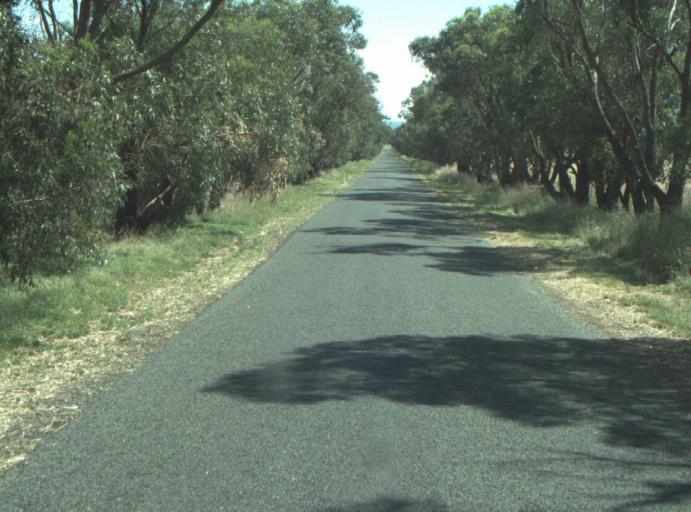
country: AU
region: Victoria
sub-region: Greater Geelong
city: Leopold
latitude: -38.1731
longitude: 144.4714
